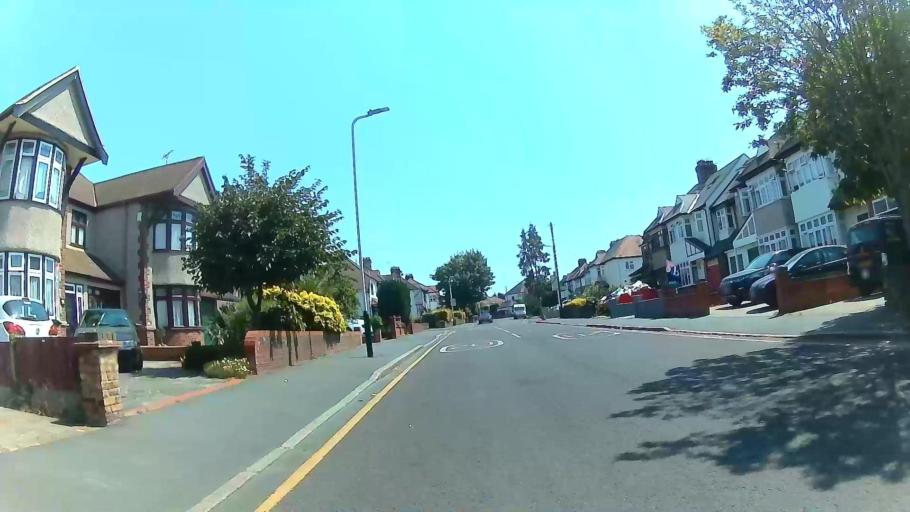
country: GB
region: England
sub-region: Greater London
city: Upminster
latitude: 51.5530
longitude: 0.2390
